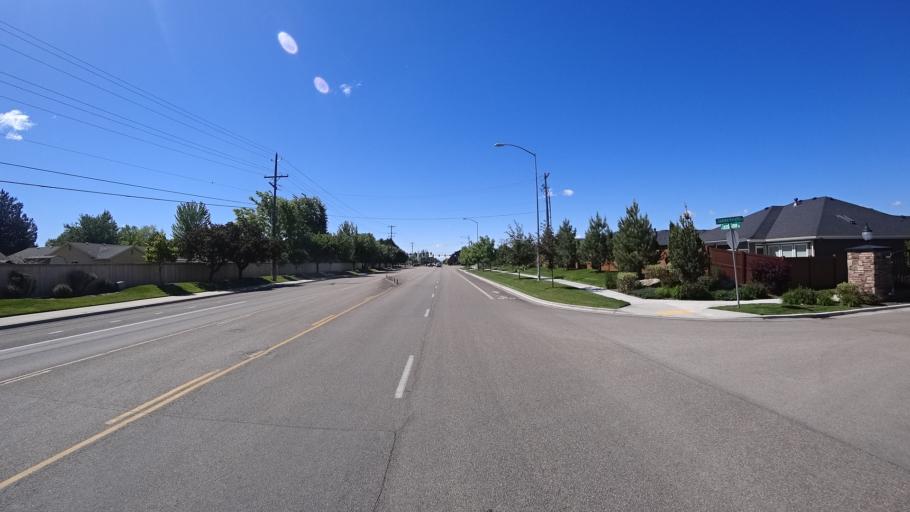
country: US
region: Idaho
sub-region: Ada County
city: Meridian
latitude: 43.6356
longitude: -116.3746
